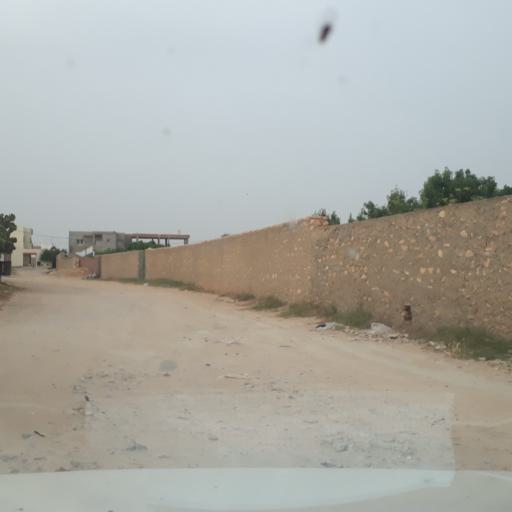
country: TN
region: Safaqis
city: Al Qarmadah
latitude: 34.8201
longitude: 10.7737
